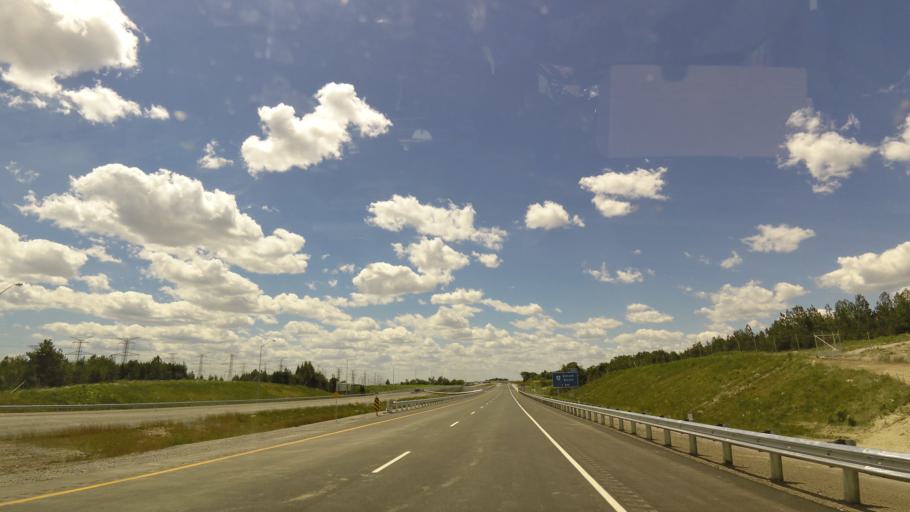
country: CA
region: Ontario
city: Oshawa
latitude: 43.9777
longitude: -78.8868
